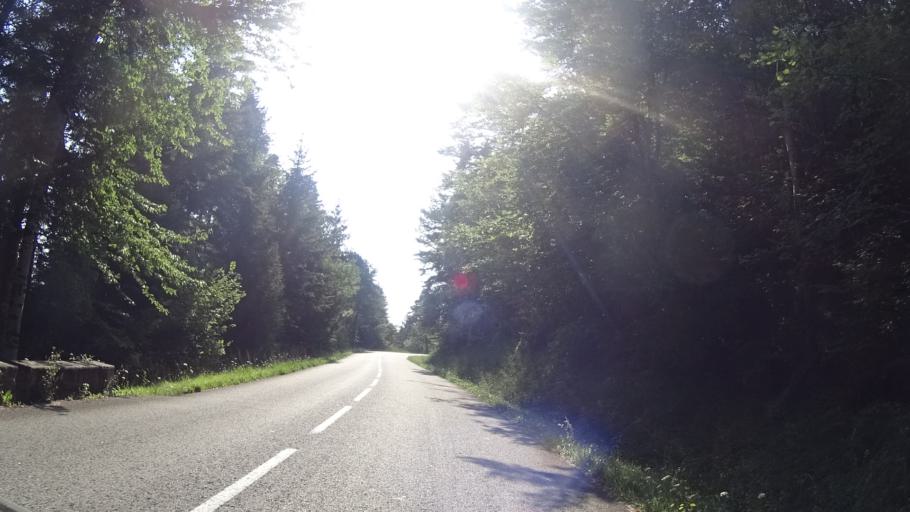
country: FR
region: Midi-Pyrenees
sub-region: Departement de l'Ariege
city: Belesta
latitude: 42.9116
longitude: 1.9945
